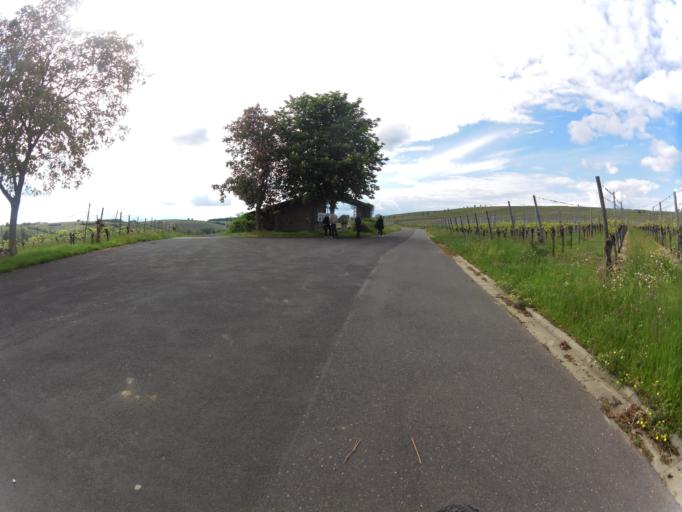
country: DE
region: Bavaria
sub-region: Regierungsbezirk Unterfranken
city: Sommerach
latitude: 49.8324
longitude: 10.1982
